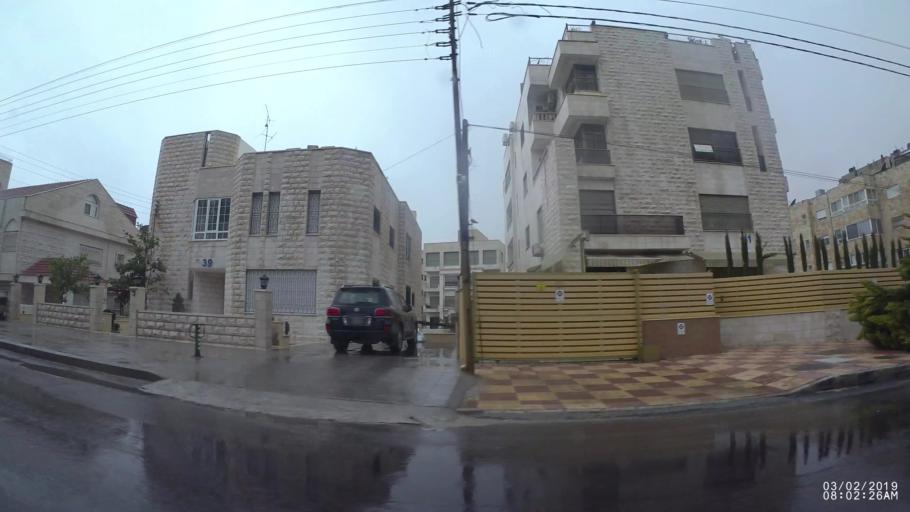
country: JO
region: Amman
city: Wadi as Sir
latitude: 31.9654
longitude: 35.8644
